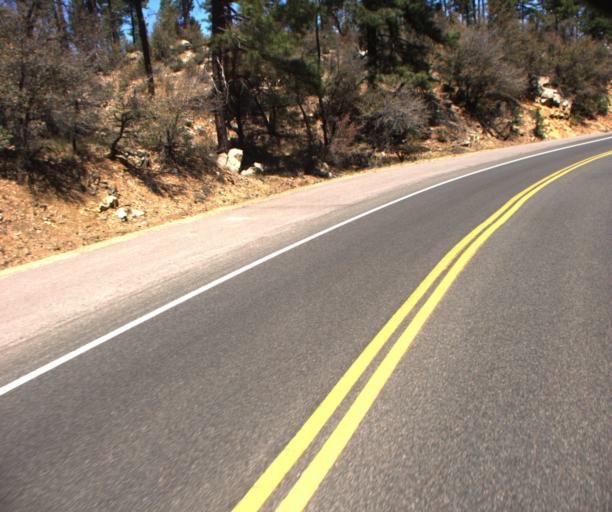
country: US
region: Arizona
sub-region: Yavapai County
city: Prescott
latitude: 34.5097
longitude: -112.4787
